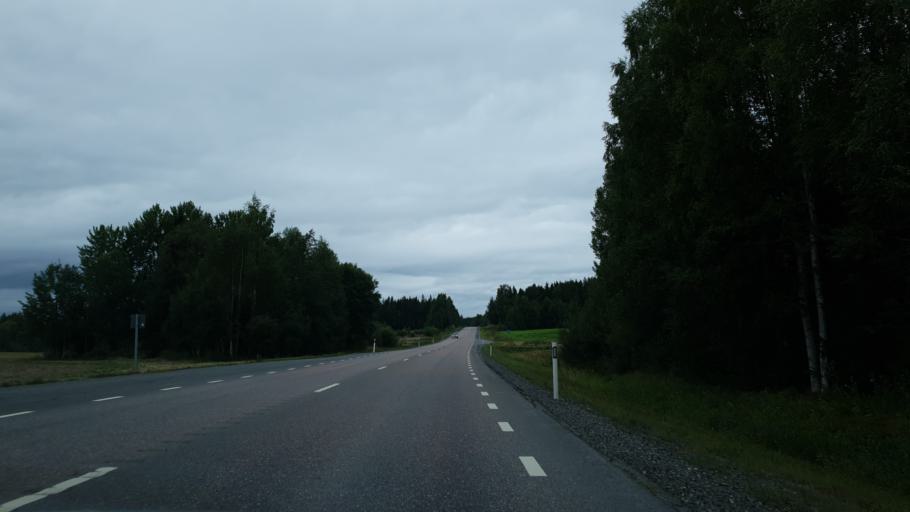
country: SE
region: Vaesterbotten
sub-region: Skelleftea Kommun
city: Viken
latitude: 64.7717
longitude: 20.8430
